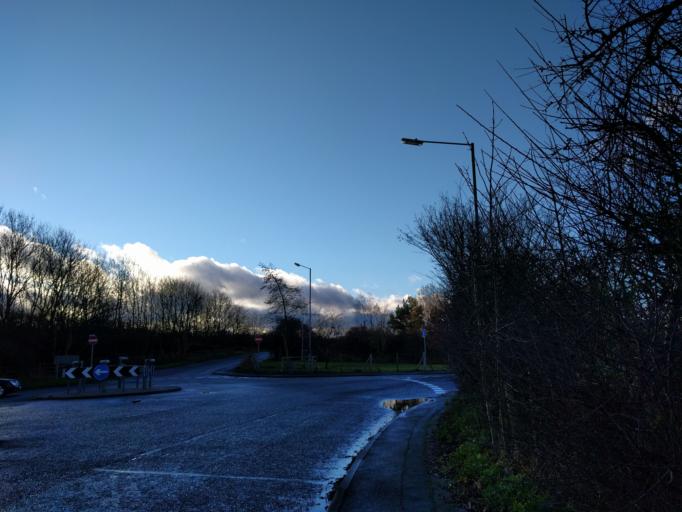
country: GB
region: England
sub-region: Northumberland
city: Cramlington
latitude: 55.1044
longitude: -1.5739
